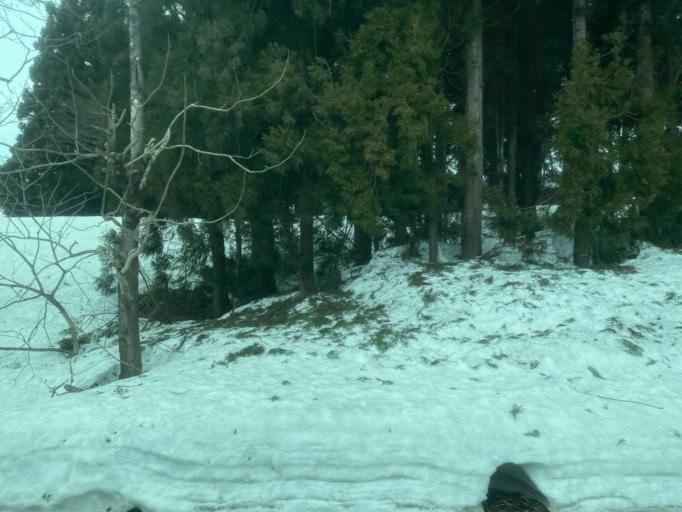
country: JP
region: Niigata
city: Shiozawa
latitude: 37.0382
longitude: 138.8412
